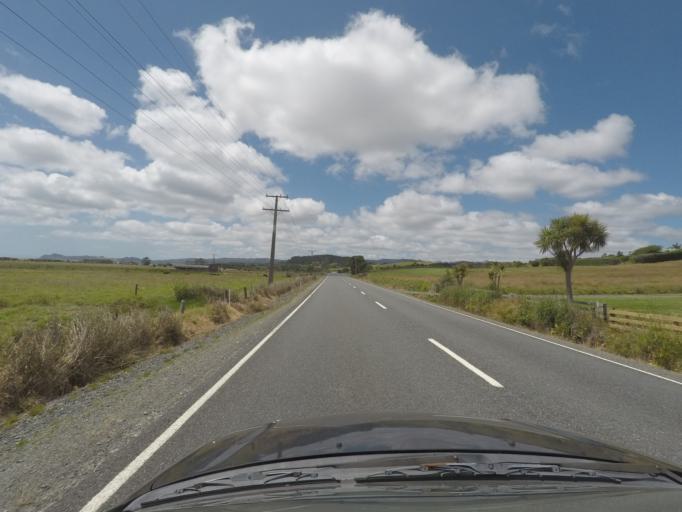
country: NZ
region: Northland
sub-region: Whangarei
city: Ruakaka
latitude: -36.0083
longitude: 174.4802
